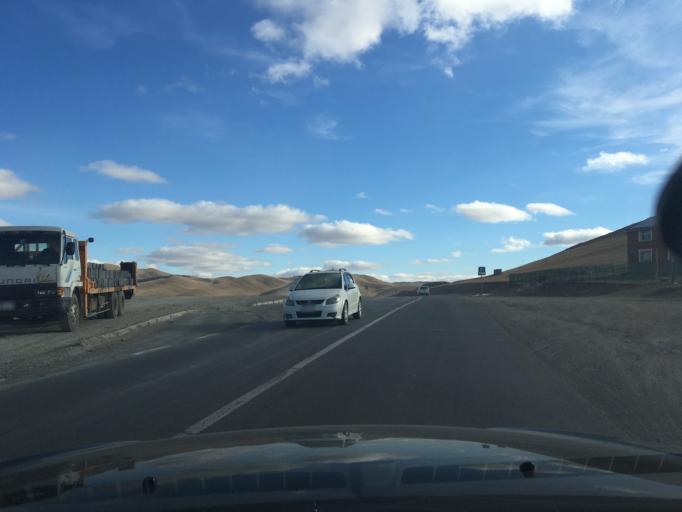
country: MN
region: Ulaanbaatar
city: Ulaanbaatar
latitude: 47.7893
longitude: 106.7465
